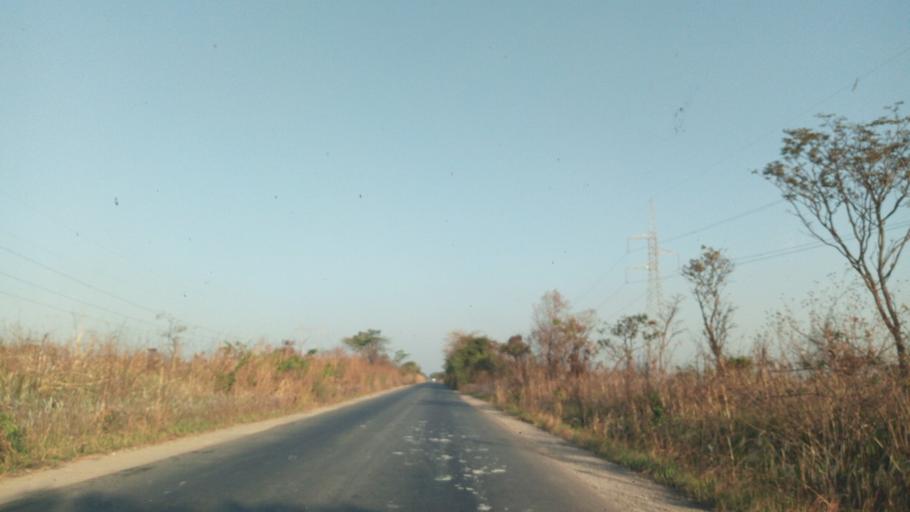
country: CD
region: Katanga
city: Likasi
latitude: -11.1099
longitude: 27.0218
